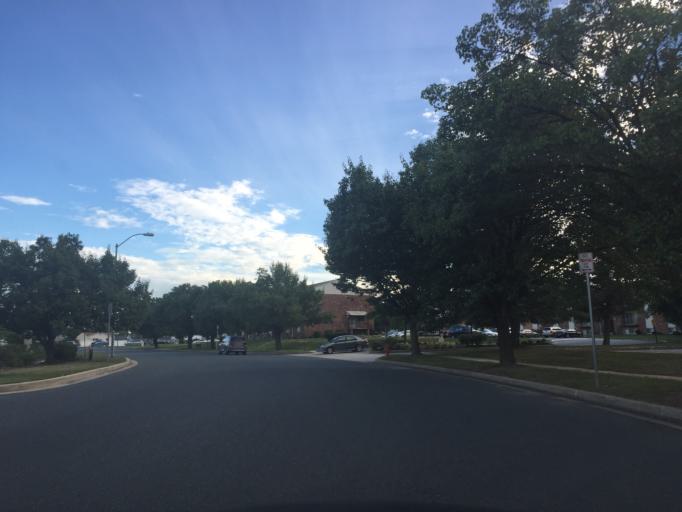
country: US
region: Maryland
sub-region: Baltimore County
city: Middle River
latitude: 39.3353
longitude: -76.4501
